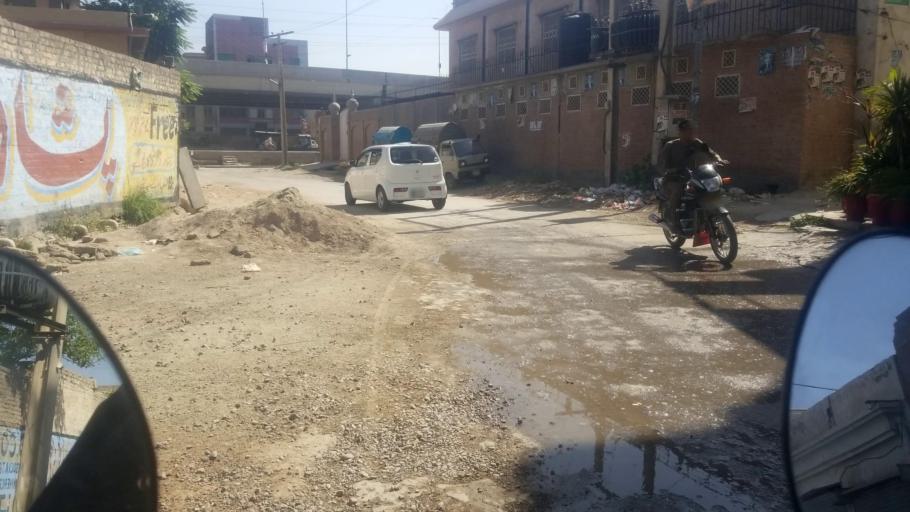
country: PK
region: Khyber Pakhtunkhwa
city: Peshawar
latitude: 34.0161
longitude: 71.5857
